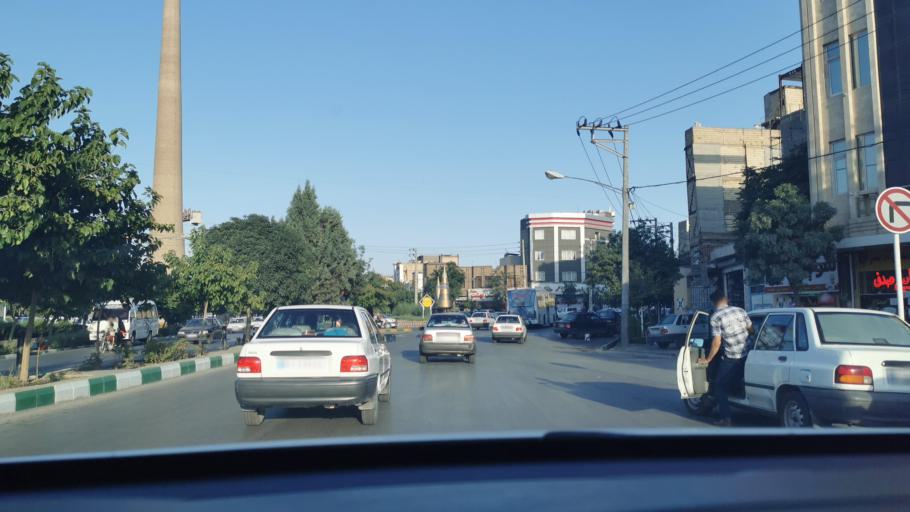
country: IR
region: Razavi Khorasan
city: Mashhad
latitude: 36.2904
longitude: 59.6495
